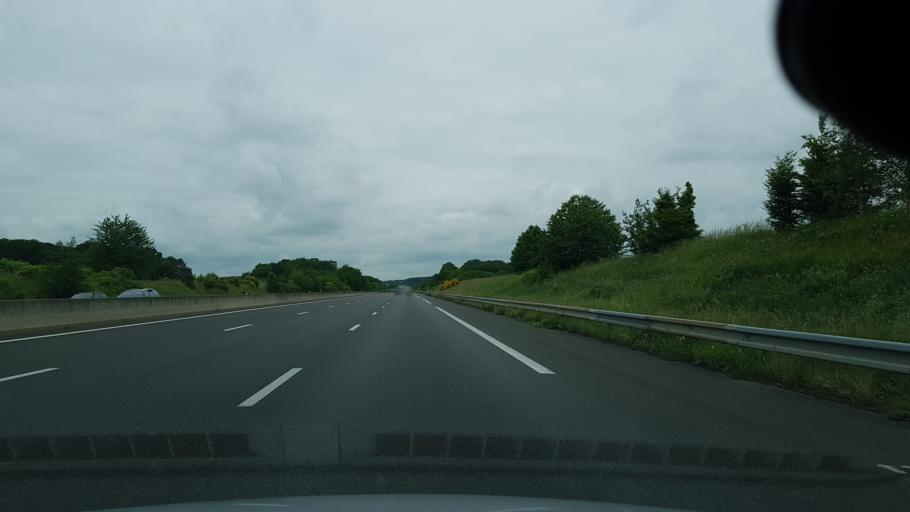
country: FR
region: Centre
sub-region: Departement du Loir-et-Cher
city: Saint-Sulpice-de-Pommeray
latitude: 47.6172
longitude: 1.2774
